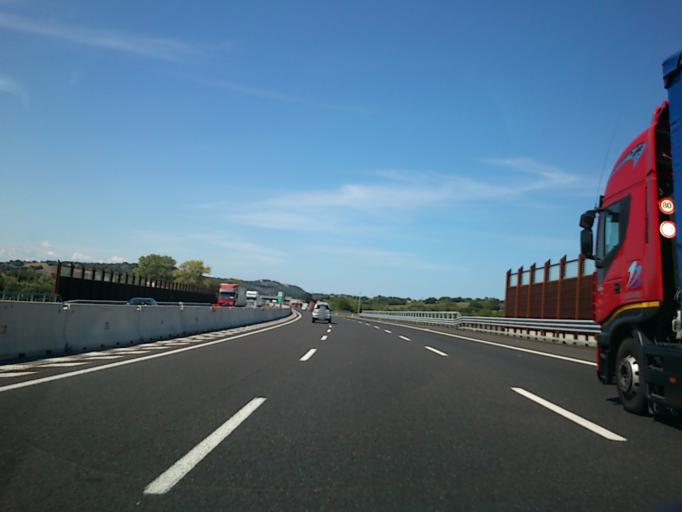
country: IT
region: The Marches
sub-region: Provincia di Pesaro e Urbino
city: Centinarola
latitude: 43.8370
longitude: 12.9907
